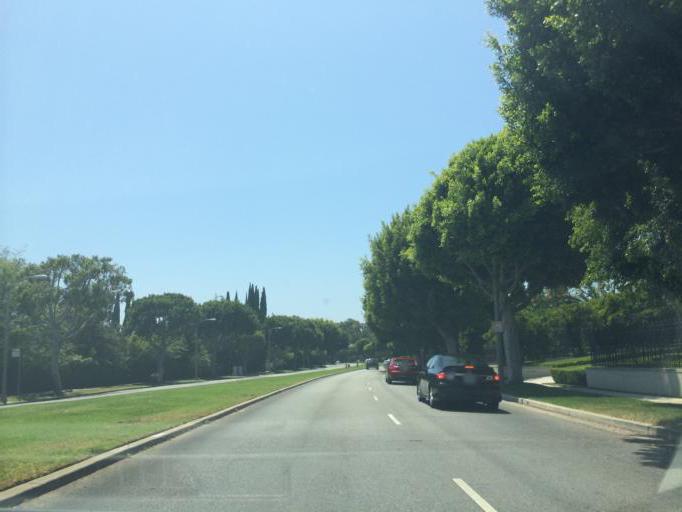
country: US
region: California
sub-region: Los Angeles County
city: Beverly Hills
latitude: 34.0866
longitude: -118.4022
